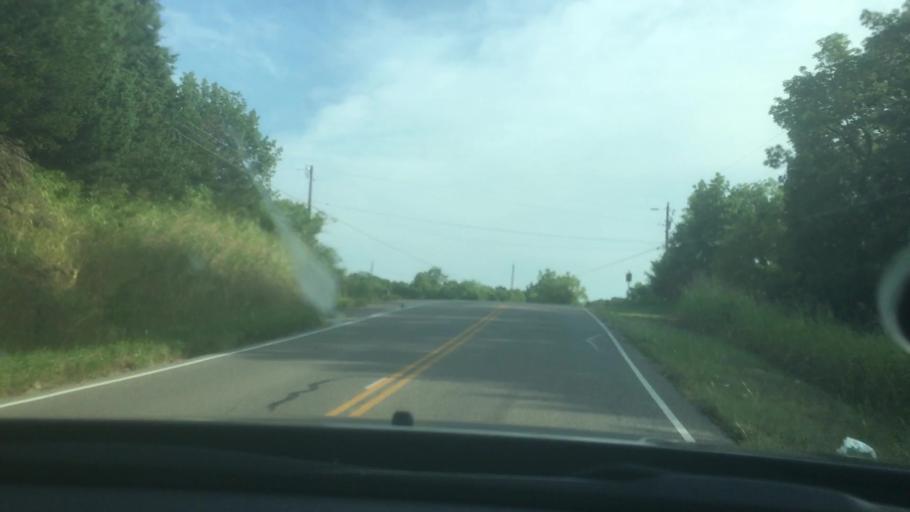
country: US
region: Oklahoma
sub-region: Pontotoc County
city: Ada
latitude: 34.7322
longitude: -96.6700
